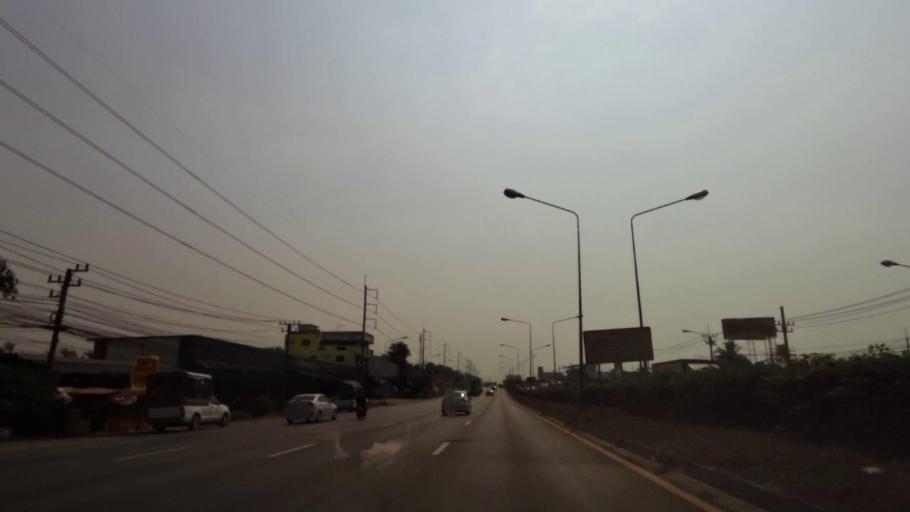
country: TH
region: Chon Buri
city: Chon Buri
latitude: 13.3704
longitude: 101.0192
